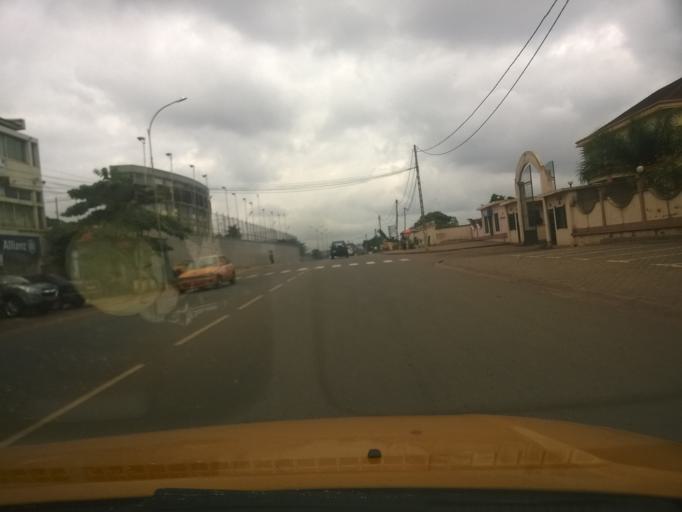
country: CM
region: Centre
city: Yaounde
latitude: 3.8770
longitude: 11.5155
